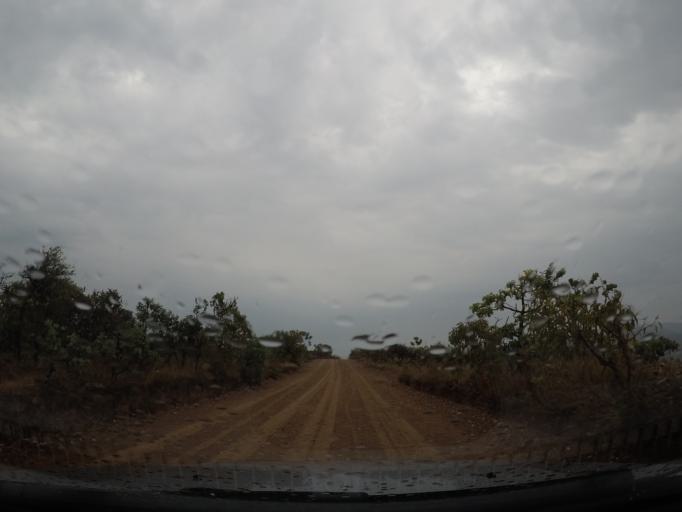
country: BR
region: Goias
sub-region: Pirenopolis
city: Pirenopolis
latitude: -15.8206
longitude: -48.9045
